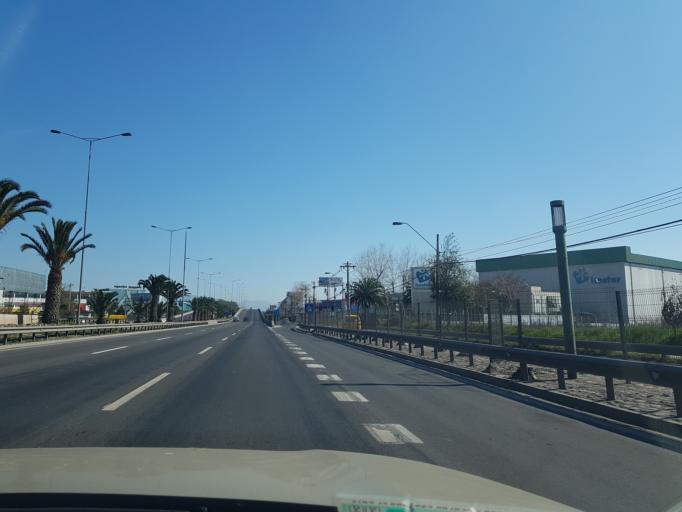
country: CL
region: Santiago Metropolitan
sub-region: Provincia de Santiago
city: Lo Prado
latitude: -33.3729
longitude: -70.7445
